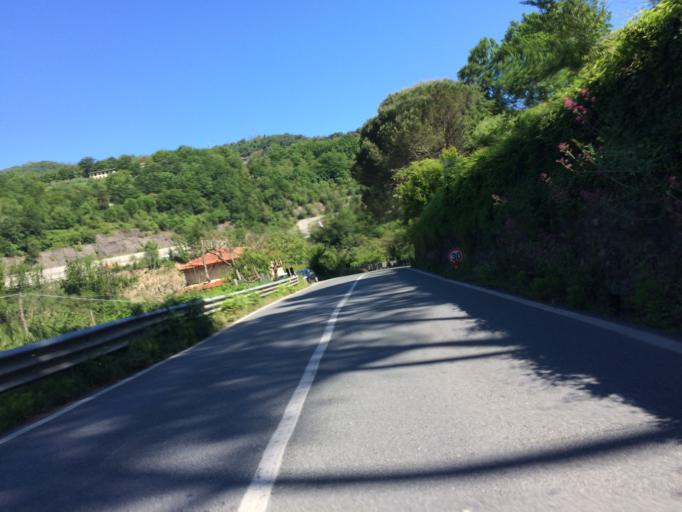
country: IT
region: Tuscany
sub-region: Provincia di Massa-Carrara
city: Montale
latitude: 44.1970
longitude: 9.9520
